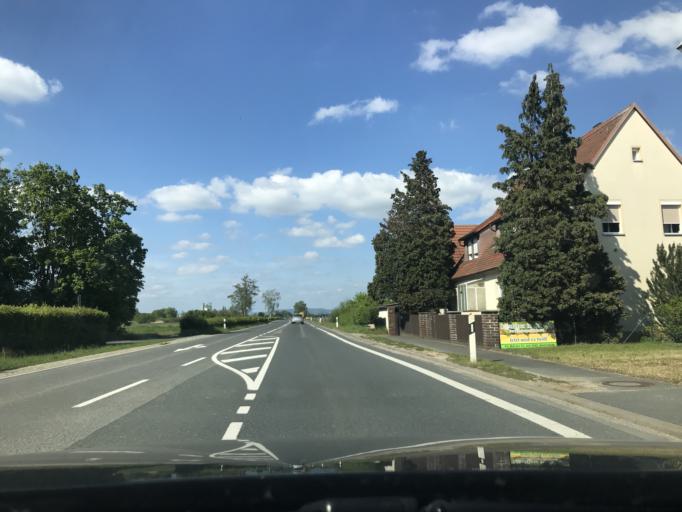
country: DE
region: Bavaria
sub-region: Regierungsbezirk Mittelfranken
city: Bubenreuth
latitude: 49.6297
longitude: 11.0116
